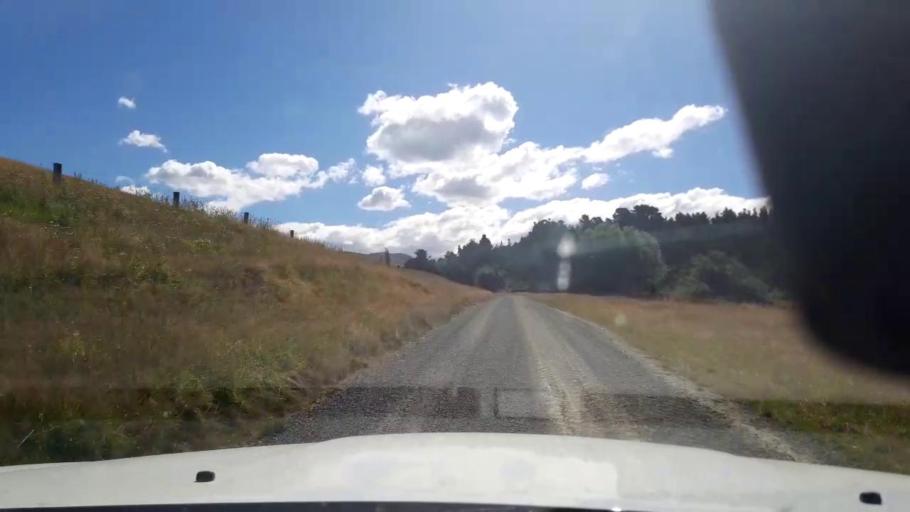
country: NZ
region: Canterbury
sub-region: Timaru District
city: Pleasant Point
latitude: -44.3111
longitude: 170.9099
